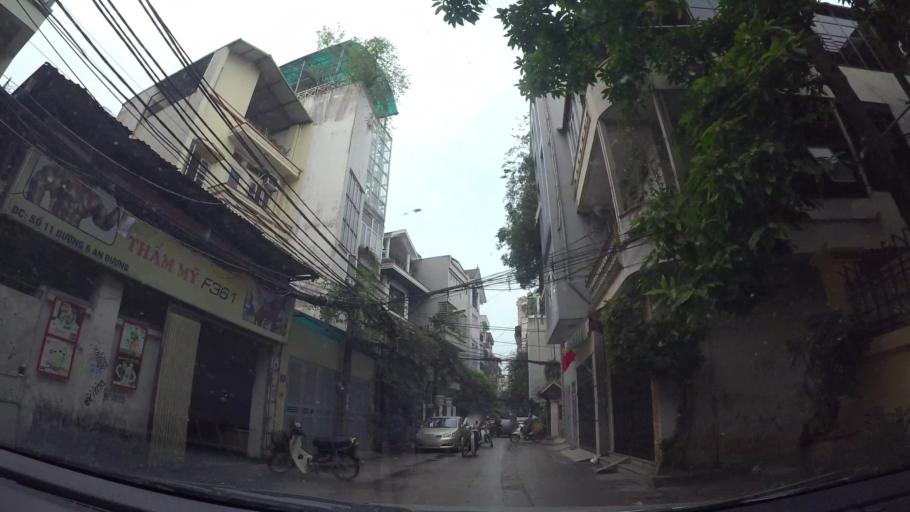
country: VN
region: Ha Noi
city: Hoan Kiem
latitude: 21.0499
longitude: 105.8439
